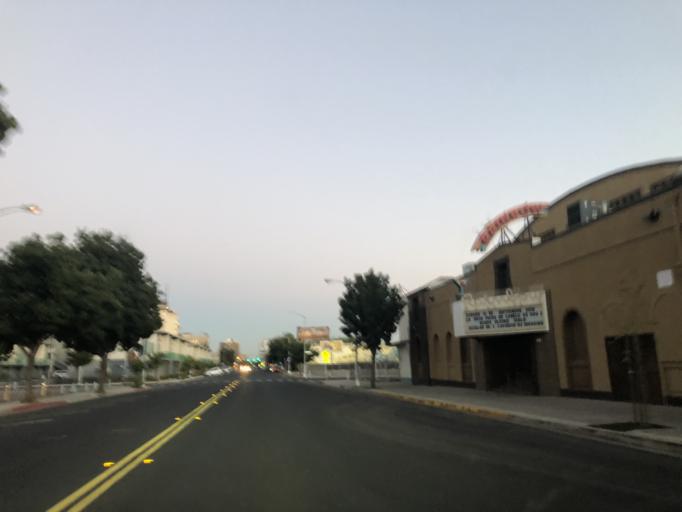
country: US
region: California
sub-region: Fresno County
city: Fresno
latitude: 36.7407
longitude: -119.7995
